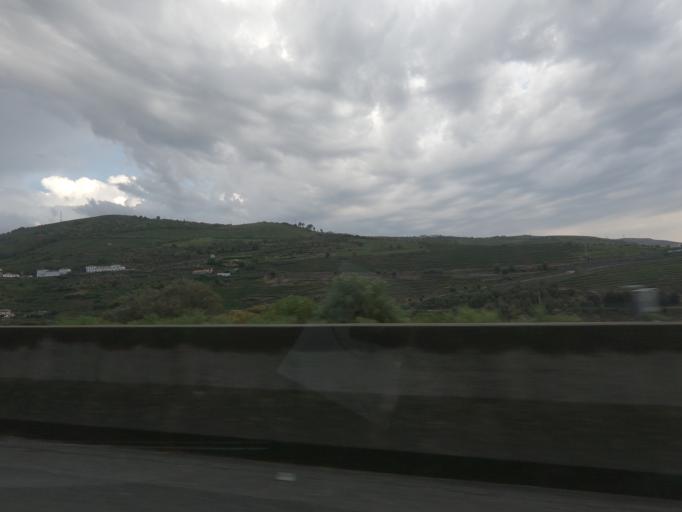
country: PT
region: Vila Real
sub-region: Peso da Regua
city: Peso da Regua
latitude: 41.1728
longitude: -7.7552
